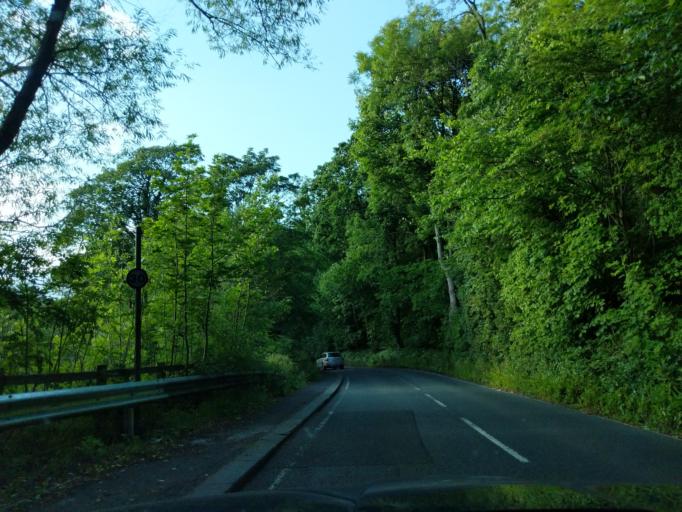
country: GB
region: England
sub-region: Northumberland
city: Bedlington
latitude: 55.1247
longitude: -1.5820
